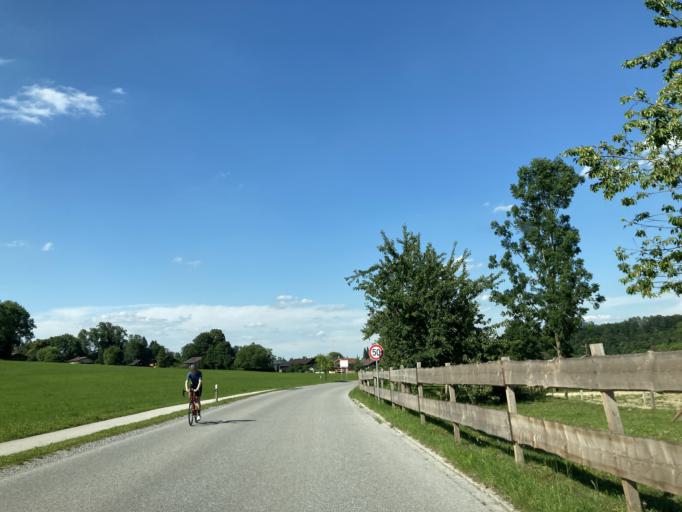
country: DE
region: Bavaria
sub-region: Upper Bavaria
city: Brannenburg
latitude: 47.7265
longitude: 12.0947
